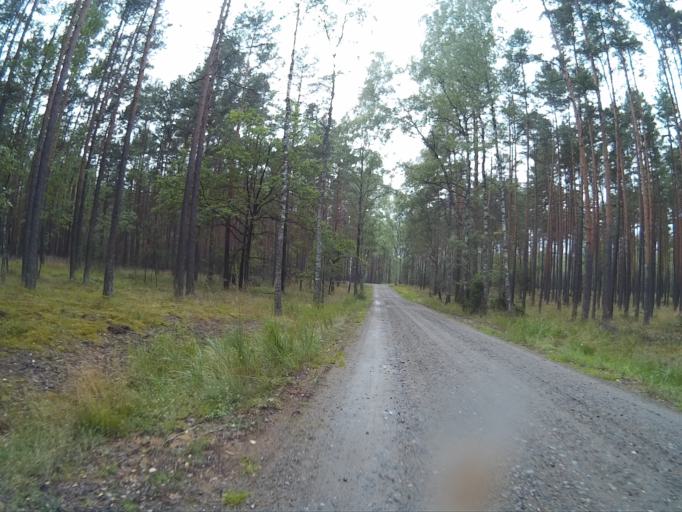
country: PL
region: Kujawsko-Pomorskie
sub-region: Powiat swiecki
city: Osie
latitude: 53.6623
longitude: 18.2786
